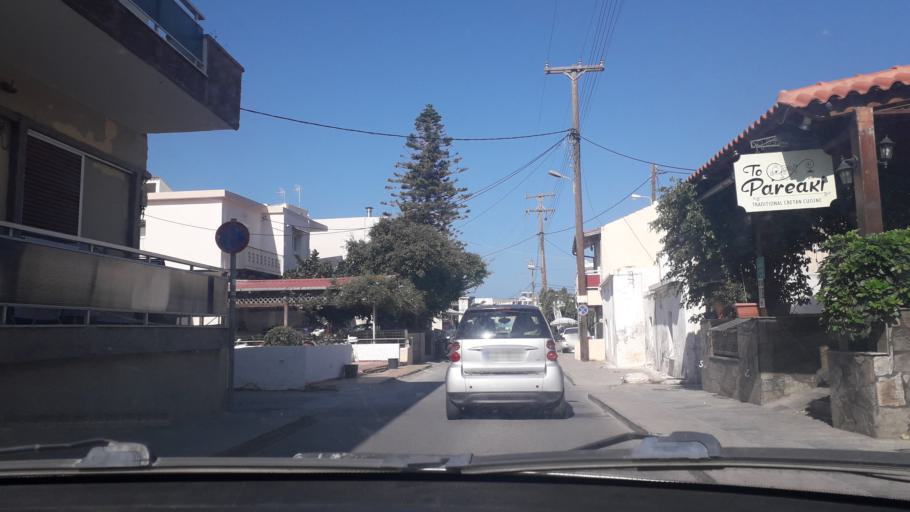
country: GR
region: Crete
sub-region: Nomos Rethymnis
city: Rethymno
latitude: 35.3666
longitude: 24.5071
